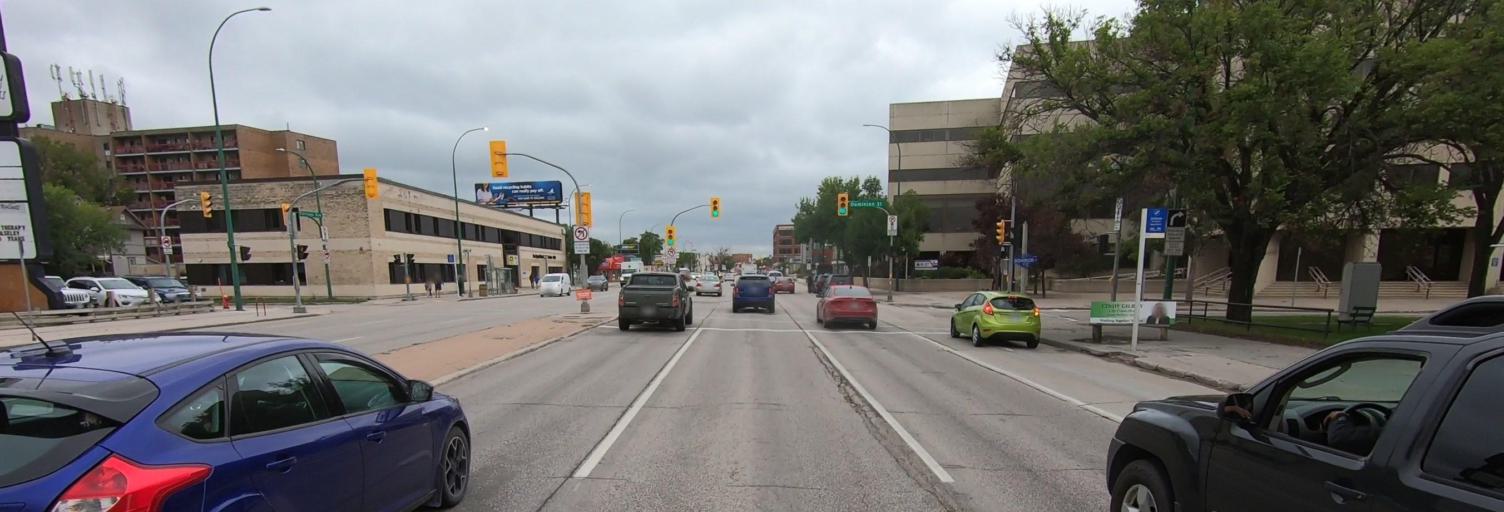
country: CA
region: Manitoba
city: Winnipeg
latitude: 49.8843
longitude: -97.1777
